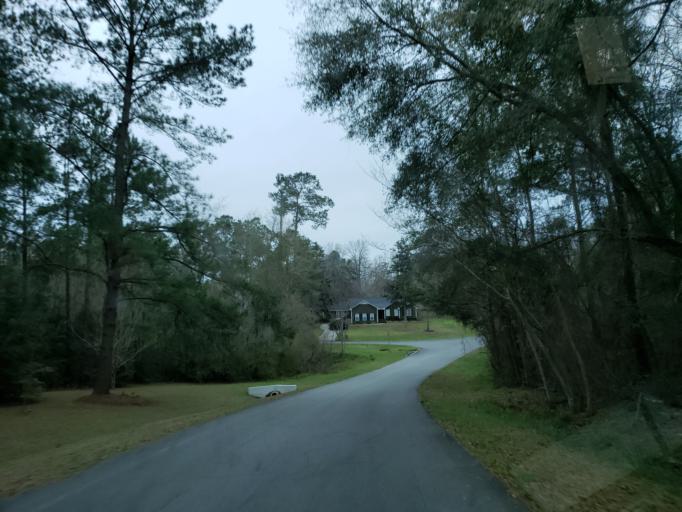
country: US
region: Georgia
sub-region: Lowndes County
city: Remerton
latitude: 30.8987
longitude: -83.3633
